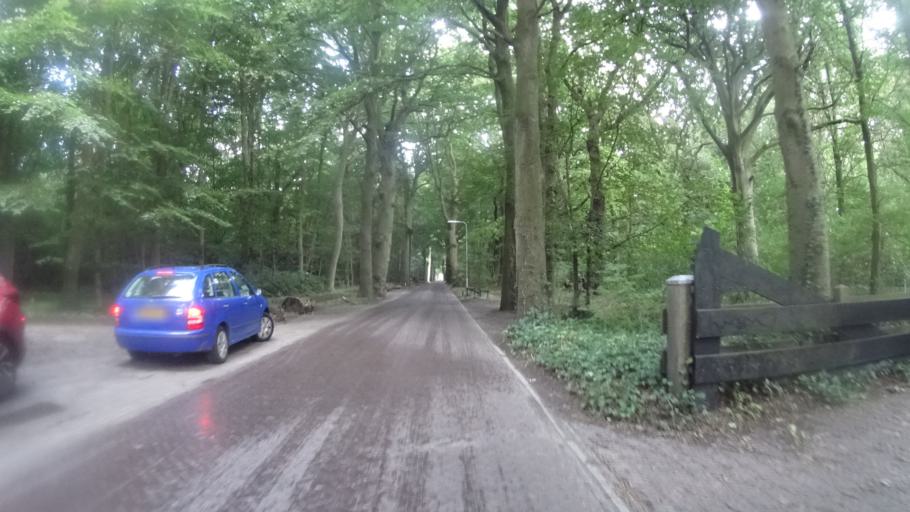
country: NL
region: North Holland
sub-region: Gemeente Heiloo
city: Heiloo
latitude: 52.6633
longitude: 4.6928
